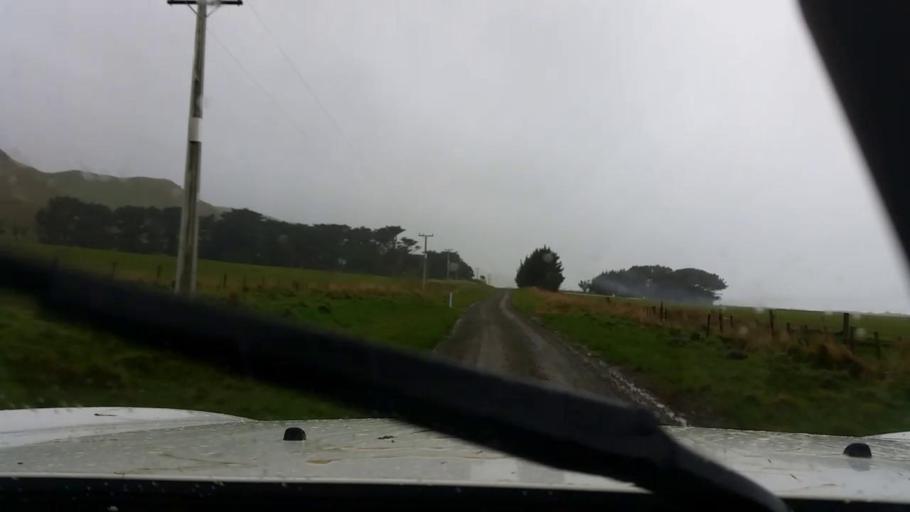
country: NZ
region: Wellington
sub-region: Masterton District
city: Masterton
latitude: -41.2591
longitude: 175.8998
